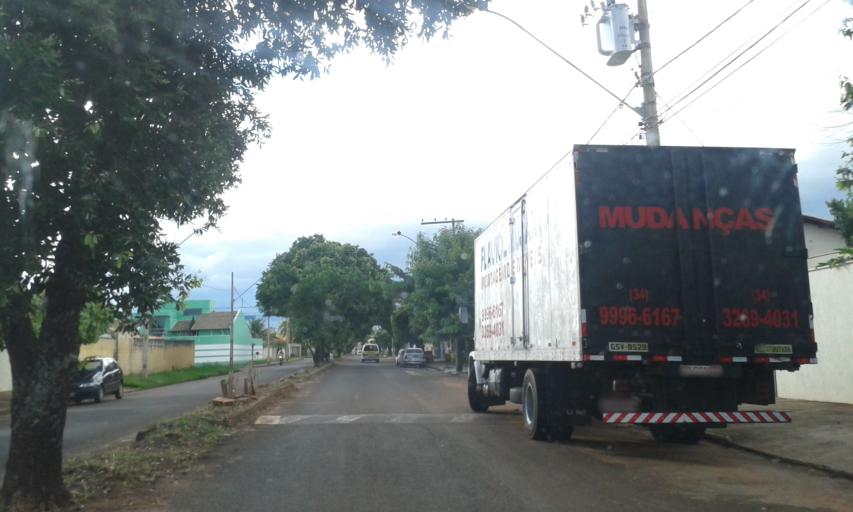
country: BR
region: Minas Gerais
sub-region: Ituiutaba
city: Ituiutaba
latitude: -18.9679
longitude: -49.4477
